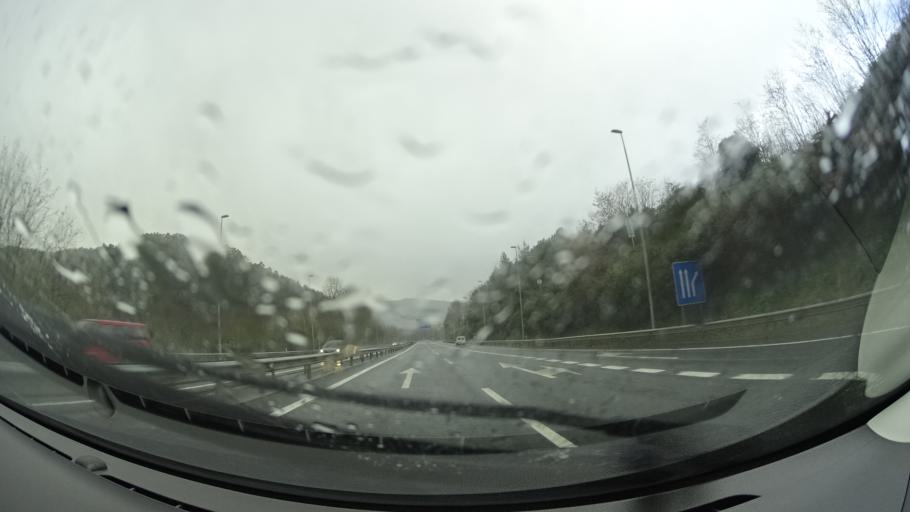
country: ES
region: Basque Country
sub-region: Bizkaia
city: Derio
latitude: 43.3128
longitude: -2.8789
